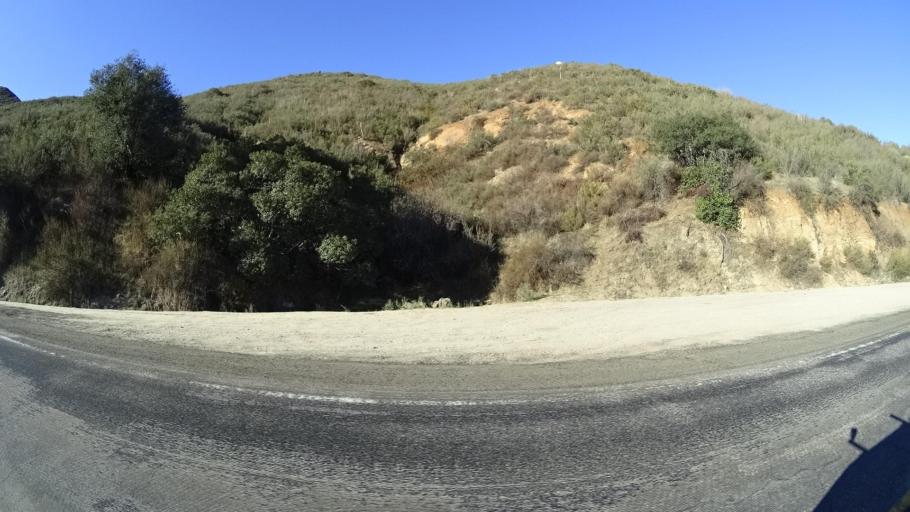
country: MX
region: Baja California
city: Tecate
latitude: 32.5936
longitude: -116.6667
